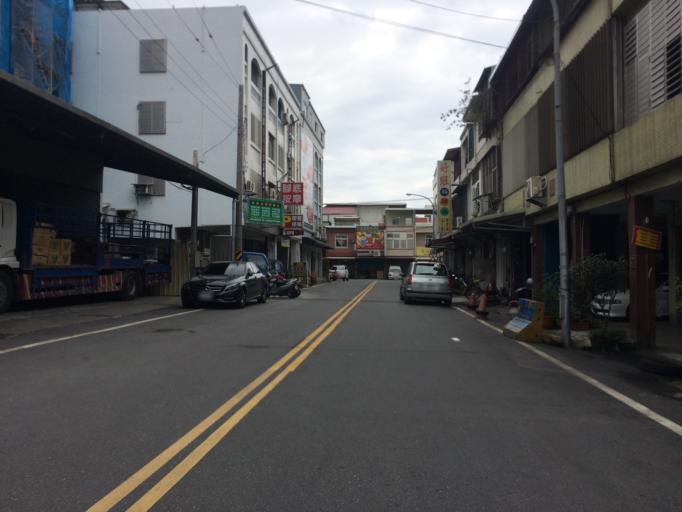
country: TW
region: Taiwan
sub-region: Hualien
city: Hualian
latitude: 23.9706
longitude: 121.6022
